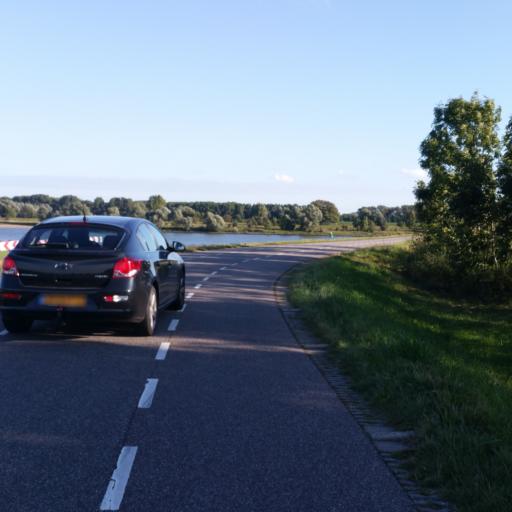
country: NL
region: Utrecht
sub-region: Gemeente Vianen
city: Vianen
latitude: 51.9967
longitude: 5.0638
